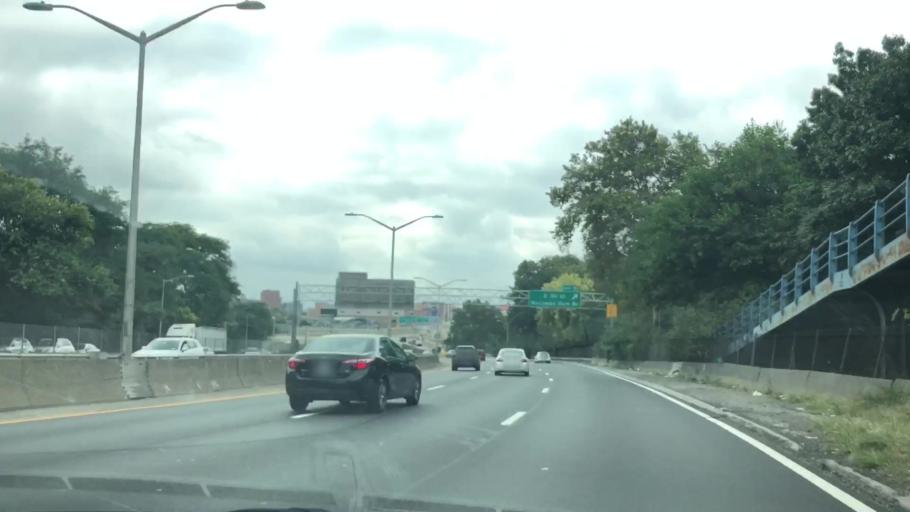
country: US
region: New York
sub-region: New York County
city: Inwood
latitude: 40.8310
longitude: -73.9323
